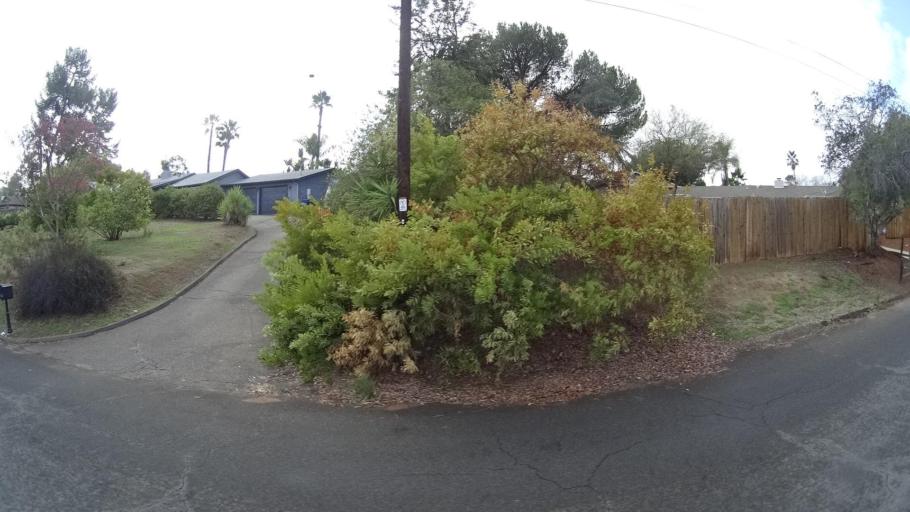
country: US
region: California
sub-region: San Diego County
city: Granite Hills
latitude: 32.7825
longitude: -116.9079
